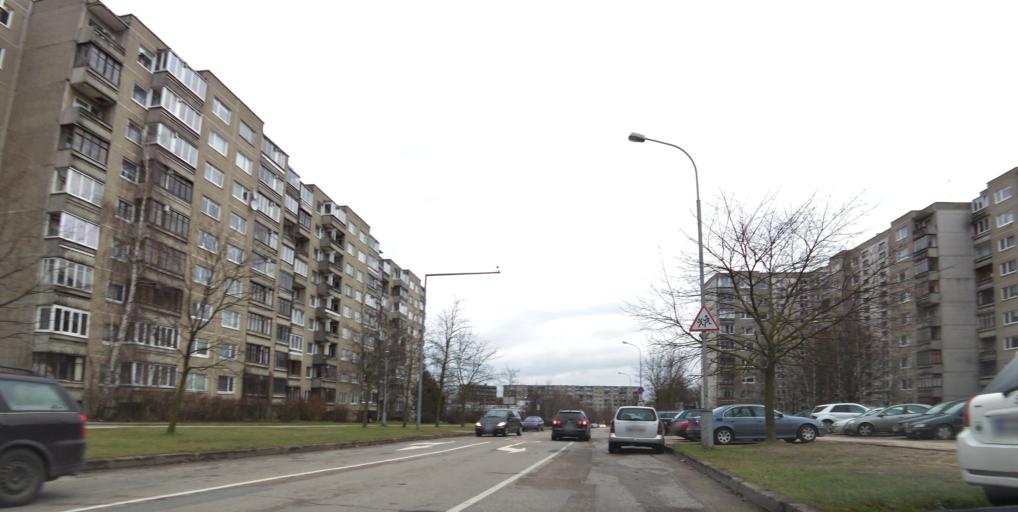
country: LT
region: Vilnius County
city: Justiniskes
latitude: 54.7211
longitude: 25.2231
